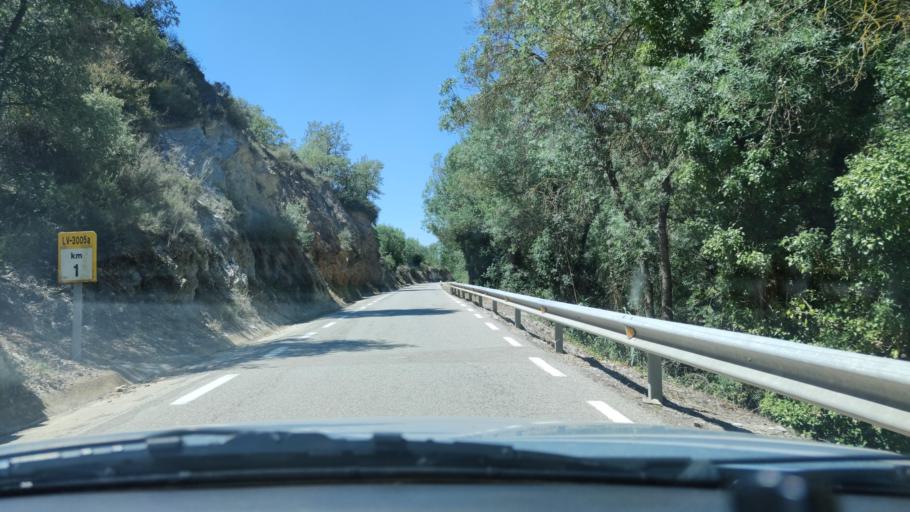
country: ES
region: Catalonia
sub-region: Provincia de Lleida
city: Tora de Riubregos
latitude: 41.8146
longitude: 1.4114
